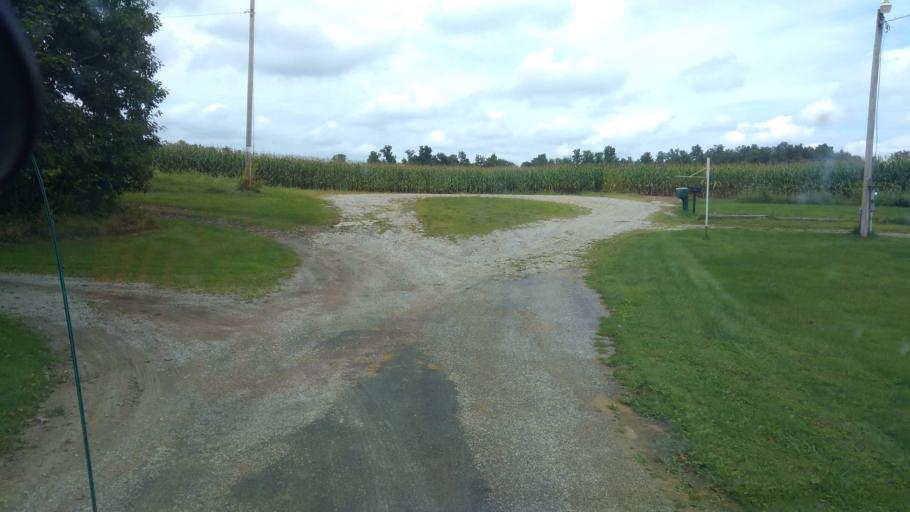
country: US
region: Ohio
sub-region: Ashland County
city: Ashland
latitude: 40.8041
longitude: -82.3692
